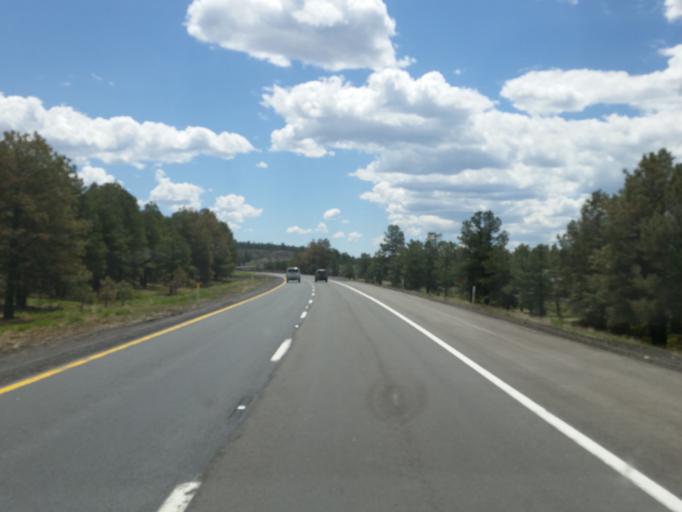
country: US
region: Arizona
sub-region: Coconino County
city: Flagstaff
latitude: 35.2165
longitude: -111.7865
